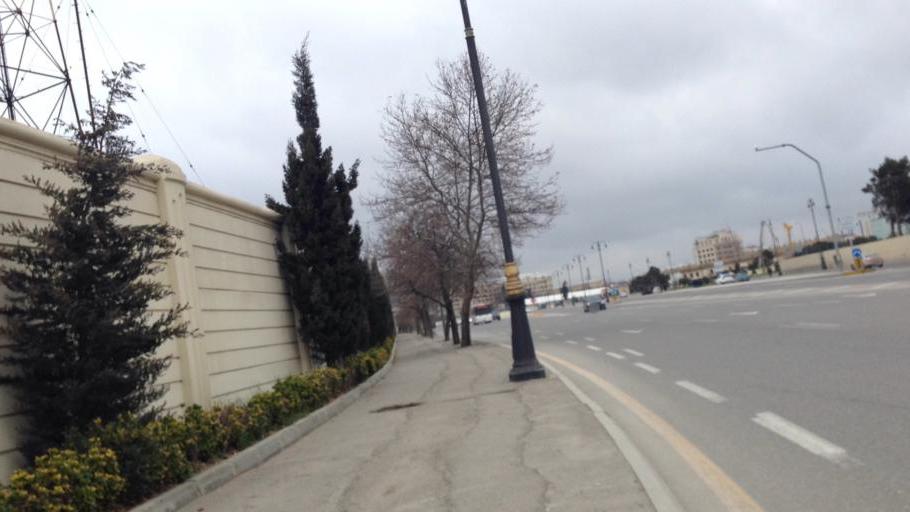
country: AZ
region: Baki
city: Baku
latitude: 40.3957
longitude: 49.8482
